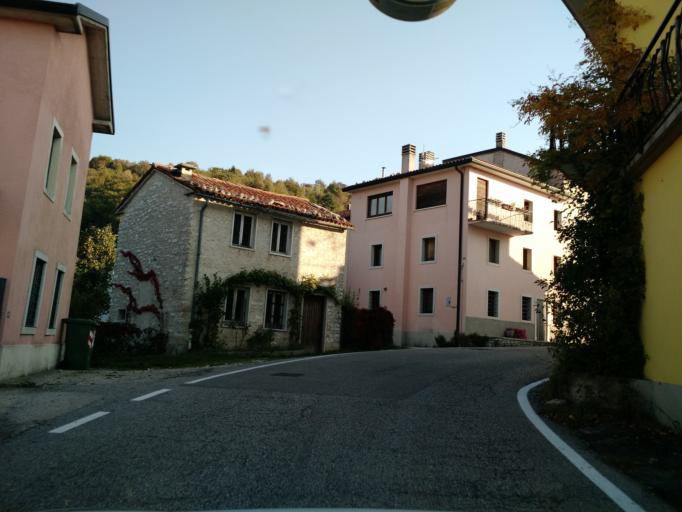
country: IT
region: Veneto
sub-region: Provincia di Vicenza
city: Lusiana
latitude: 45.7831
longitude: 11.5692
